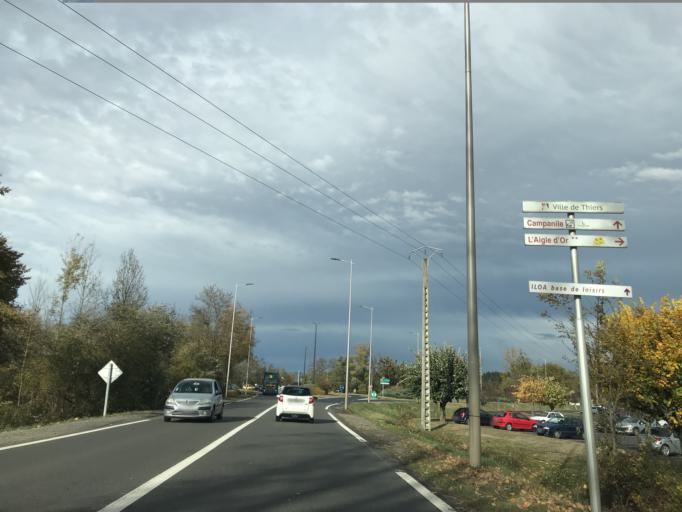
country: FR
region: Auvergne
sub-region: Departement du Puy-de-Dome
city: Peschadoires
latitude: 45.8388
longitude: 3.5065
